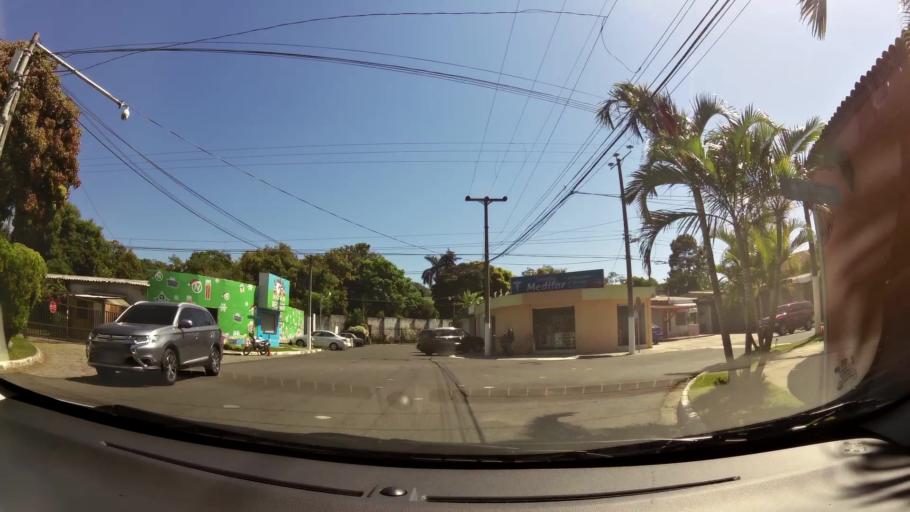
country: SV
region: La Libertad
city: Nuevo Cuscatlan
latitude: 13.6518
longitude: -89.2786
